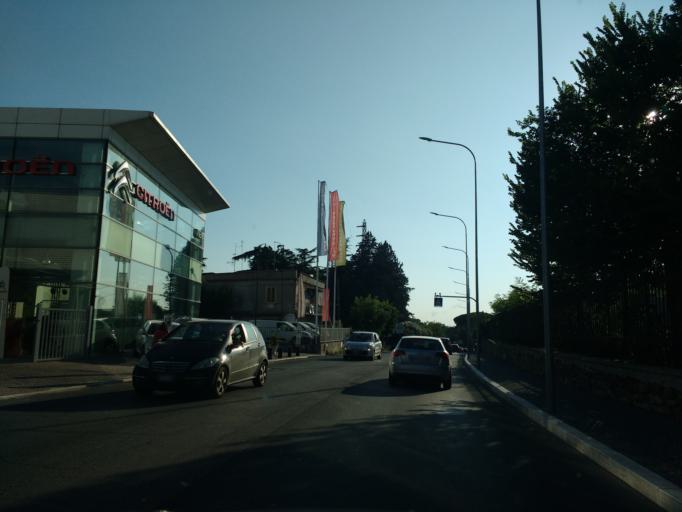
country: IT
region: Latium
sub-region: Citta metropolitana di Roma Capitale
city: Villa Adriana
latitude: 41.9554
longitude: 12.7681
